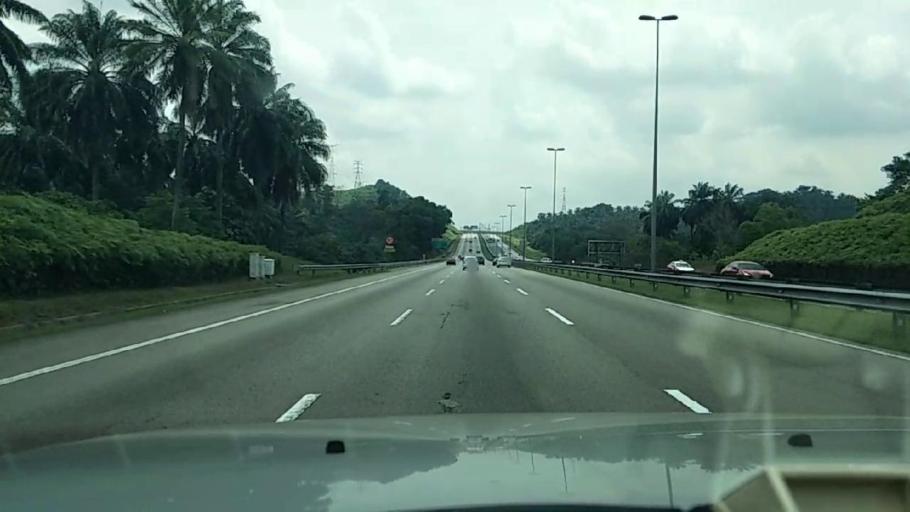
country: MY
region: Putrajaya
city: Putrajaya
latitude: 3.0013
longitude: 101.6831
